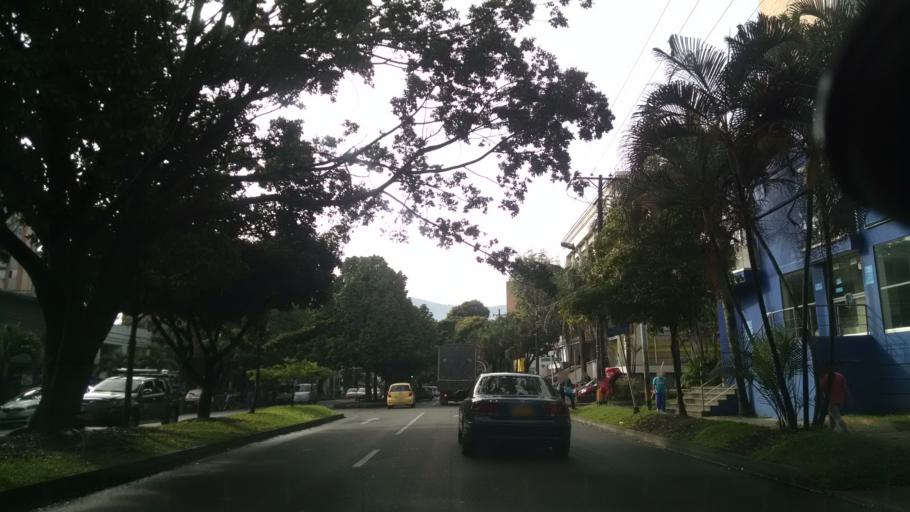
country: CO
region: Antioquia
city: Medellin
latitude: 6.2442
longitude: -75.5945
